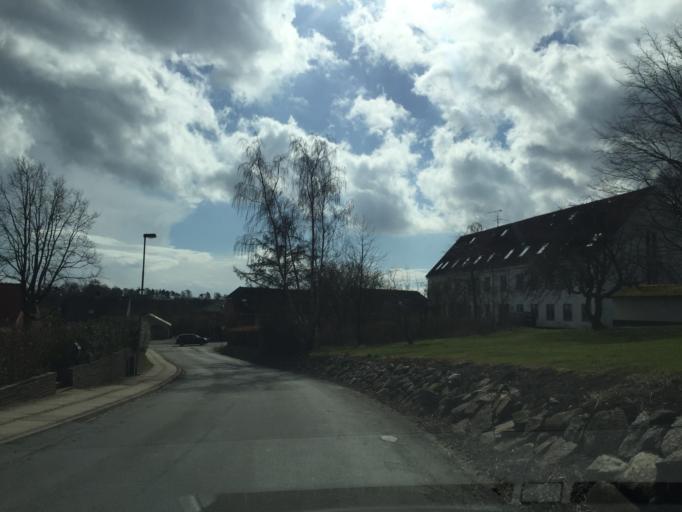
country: DK
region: South Denmark
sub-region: Svendborg Kommune
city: Svendborg
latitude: 55.0728
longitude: 10.4916
